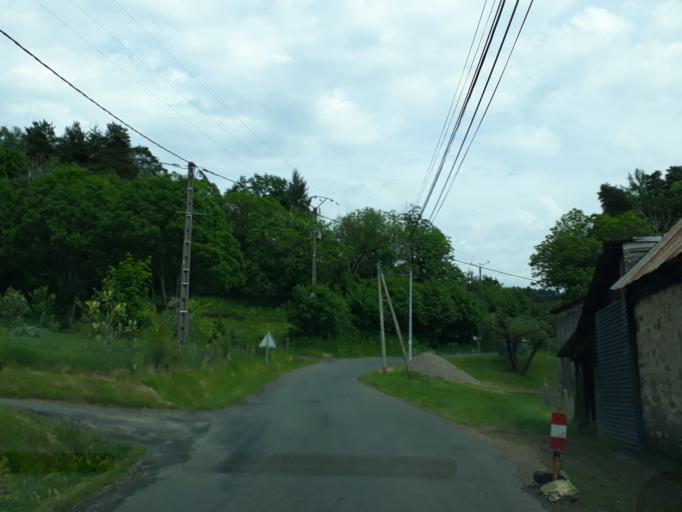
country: FR
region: Limousin
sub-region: Departement de la Correze
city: Beynat
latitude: 45.1158
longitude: 1.7613
